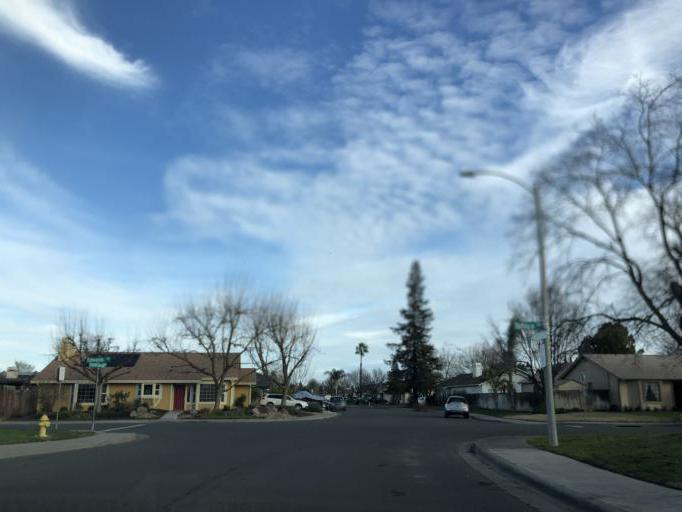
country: US
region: California
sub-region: Yolo County
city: Woodland
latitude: 38.6733
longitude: -121.7554
